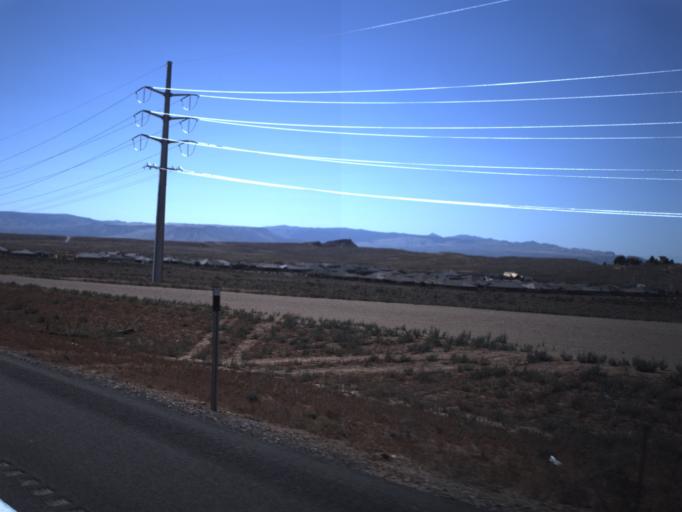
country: US
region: Utah
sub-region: Washington County
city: Washington
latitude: 37.0750
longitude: -113.4857
